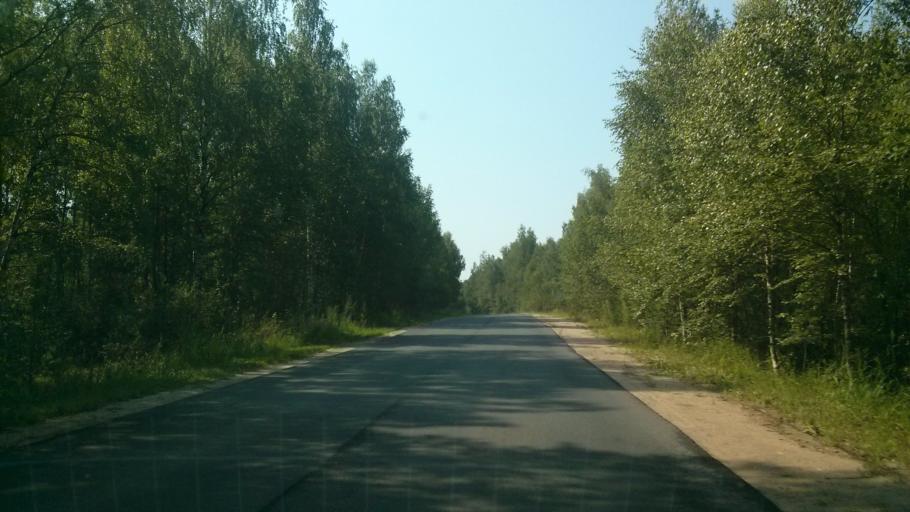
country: RU
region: Vladimir
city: Murom
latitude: 55.5208
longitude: 42.0209
